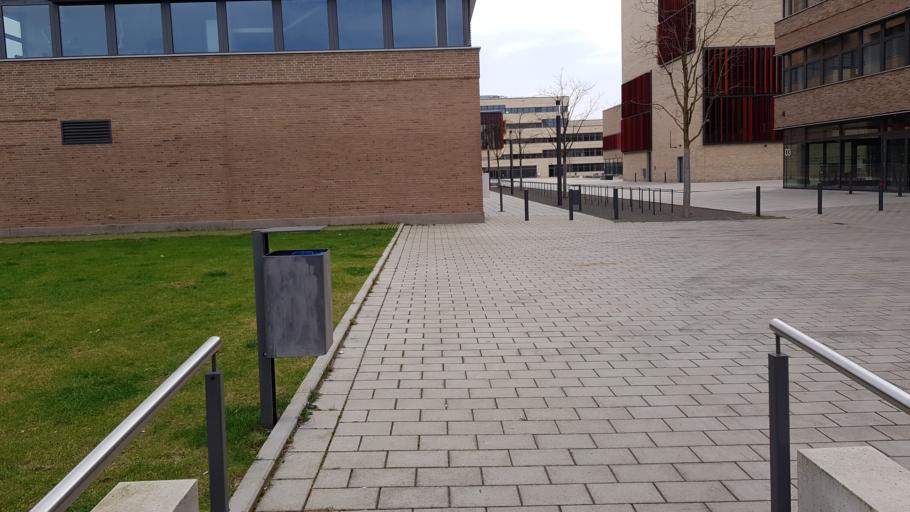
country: DE
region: North Rhine-Westphalia
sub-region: Regierungsbezirk Dusseldorf
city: Muelheim (Ruhr)
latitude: 51.4279
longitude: 6.8565
